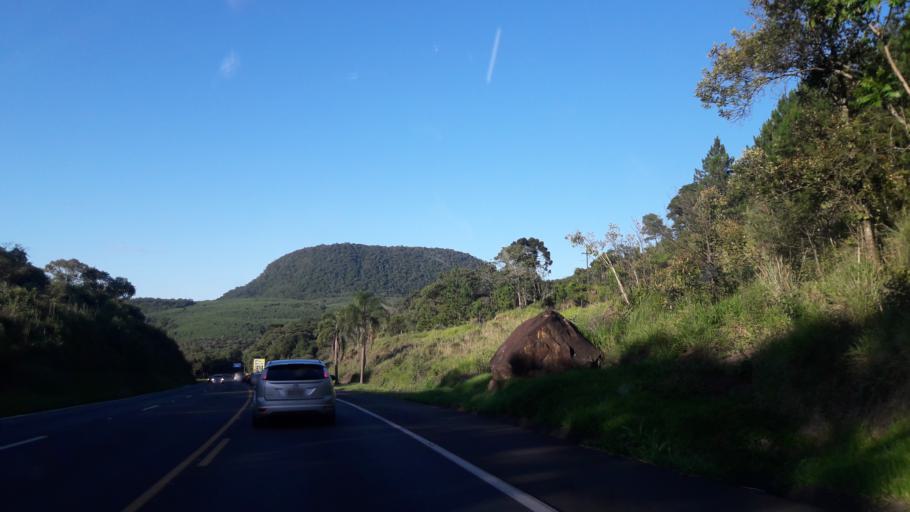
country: BR
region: Parana
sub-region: Prudentopolis
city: Prudentopolis
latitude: -25.3192
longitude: -51.1894
